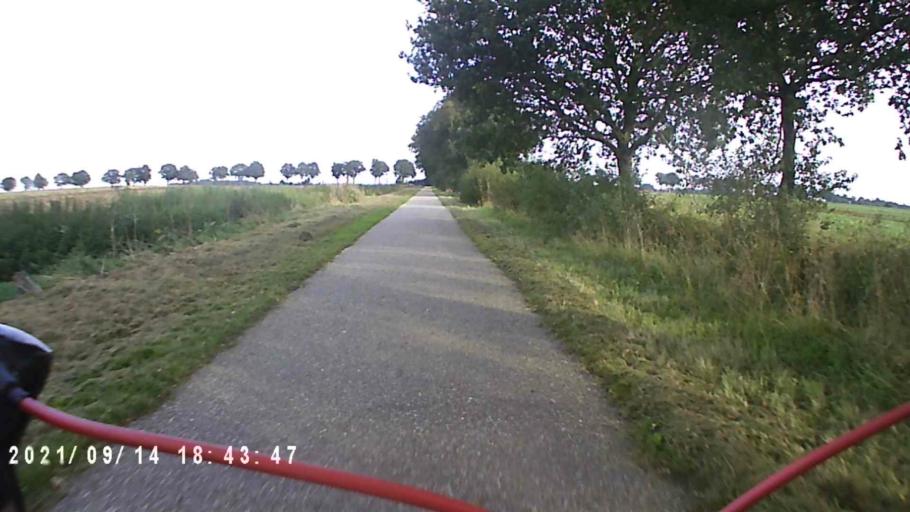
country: NL
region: Drenthe
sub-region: Gemeente Aa en Hunze
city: Anloo
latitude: 53.0226
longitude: 6.6854
